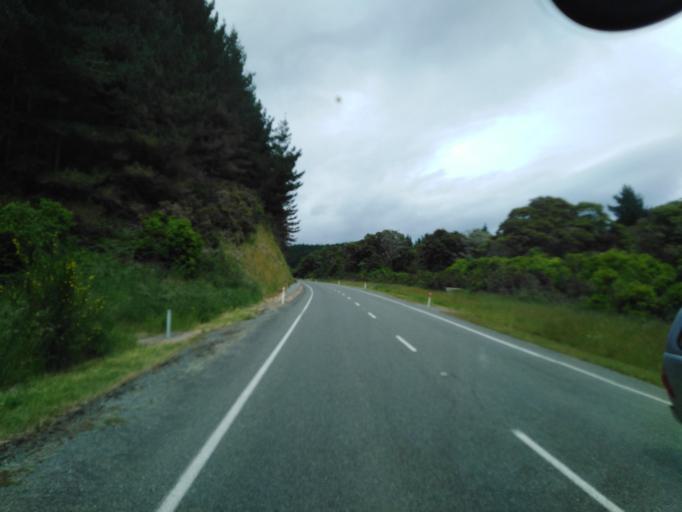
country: NZ
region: Tasman
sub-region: Tasman District
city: Wakefield
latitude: -41.4753
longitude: 172.9345
